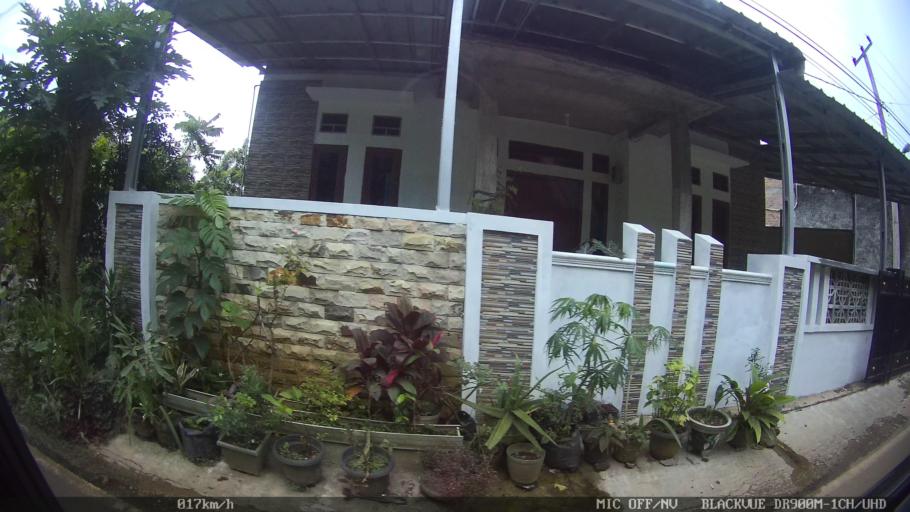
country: ID
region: Lampung
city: Kedaton
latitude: -5.3893
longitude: 105.1996
